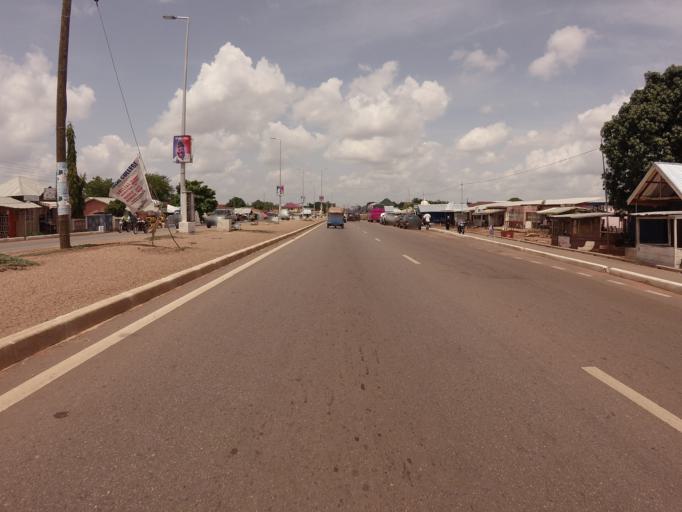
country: GH
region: Northern
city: Tamale
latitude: 9.3985
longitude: -0.8304
